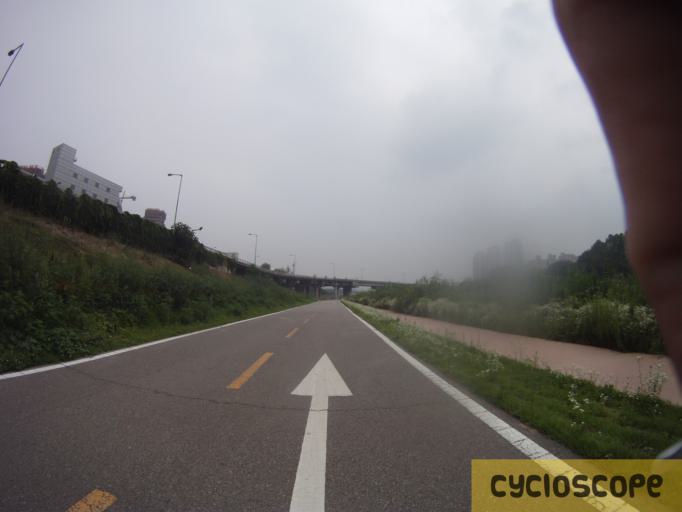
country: KR
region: Gyeonggi-do
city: Kwangmyong
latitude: 37.4598
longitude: 126.8905
